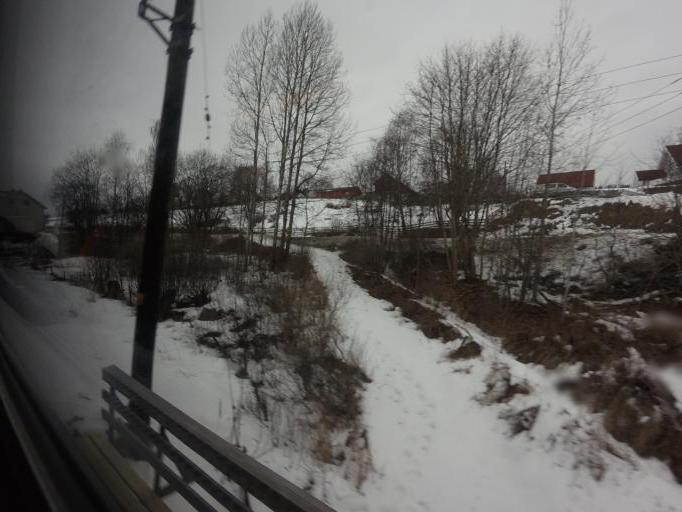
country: NO
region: Hedmark
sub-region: Ringsaker
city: Moelv
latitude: 60.9133
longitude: 10.7471
